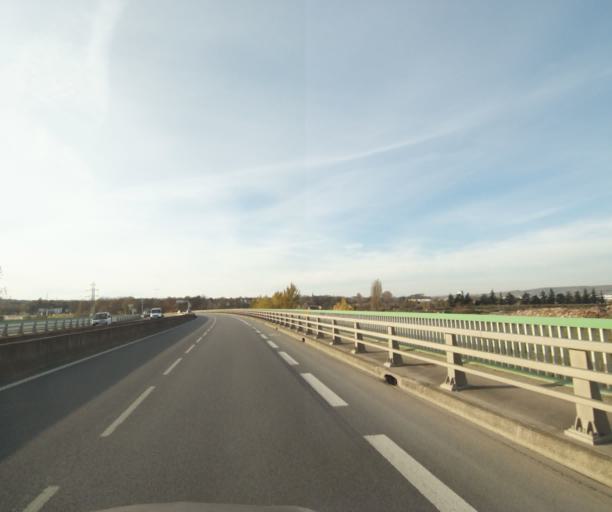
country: FR
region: Ile-de-France
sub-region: Departement des Yvelines
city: Medan
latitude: 48.9682
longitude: 1.9987
